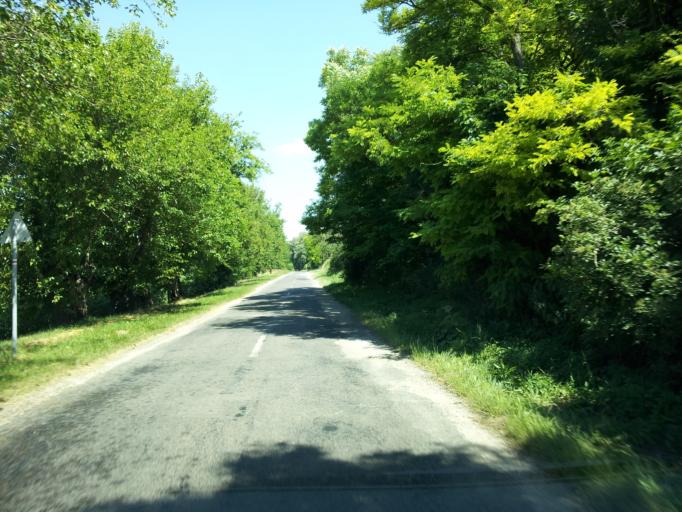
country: HU
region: Fejer
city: Many
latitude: 47.5384
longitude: 18.5907
